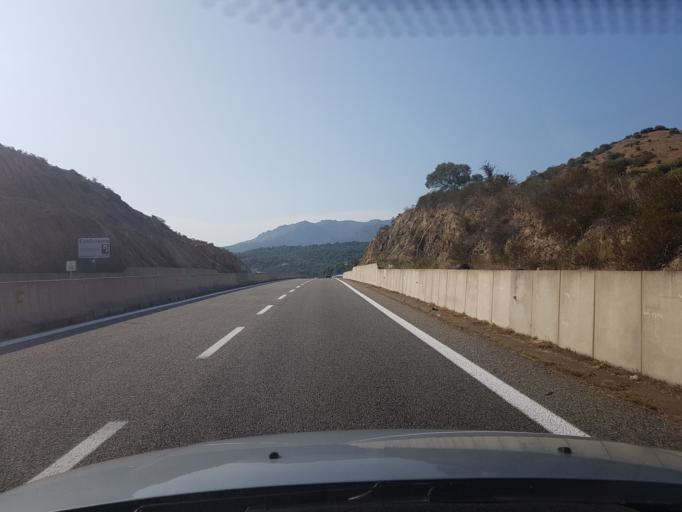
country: IT
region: Sardinia
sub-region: Provincia di Olbia-Tempio
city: Padru
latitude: 40.8220
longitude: 9.5808
